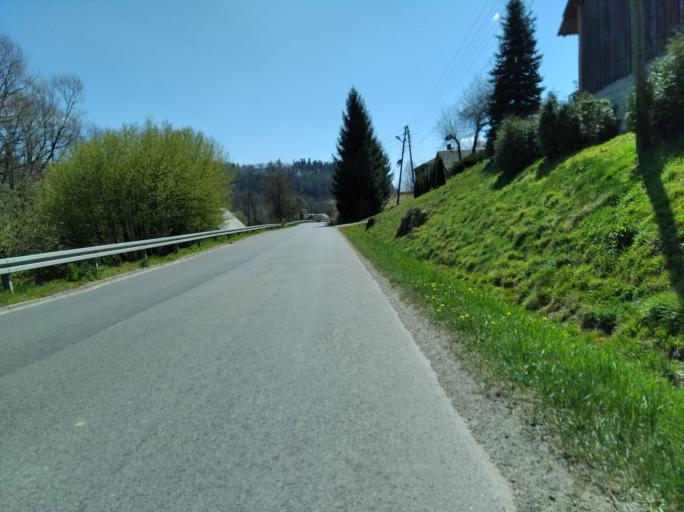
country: PL
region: Subcarpathian Voivodeship
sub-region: Powiat brzozowski
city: Dydnia
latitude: 49.6906
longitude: 22.1845
